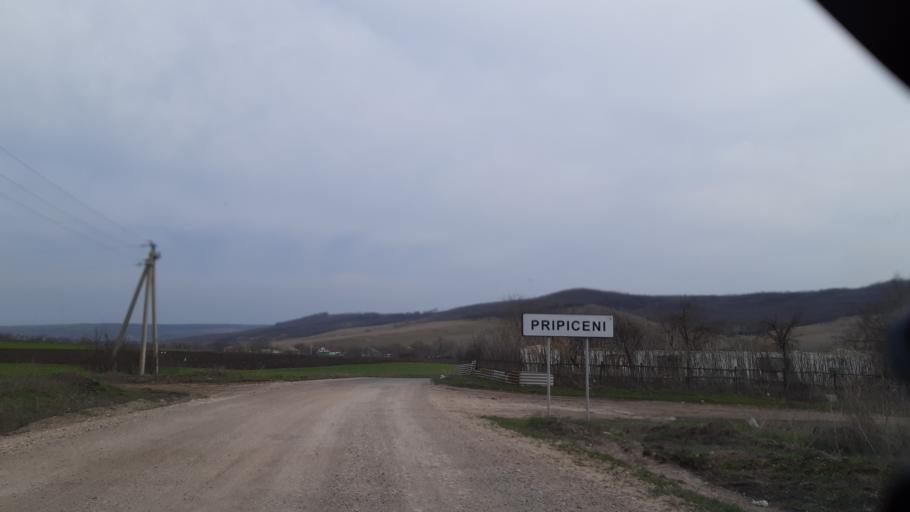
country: MD
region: Soldanesti
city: Soldanesti
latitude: 47.6888
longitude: 28.7440
